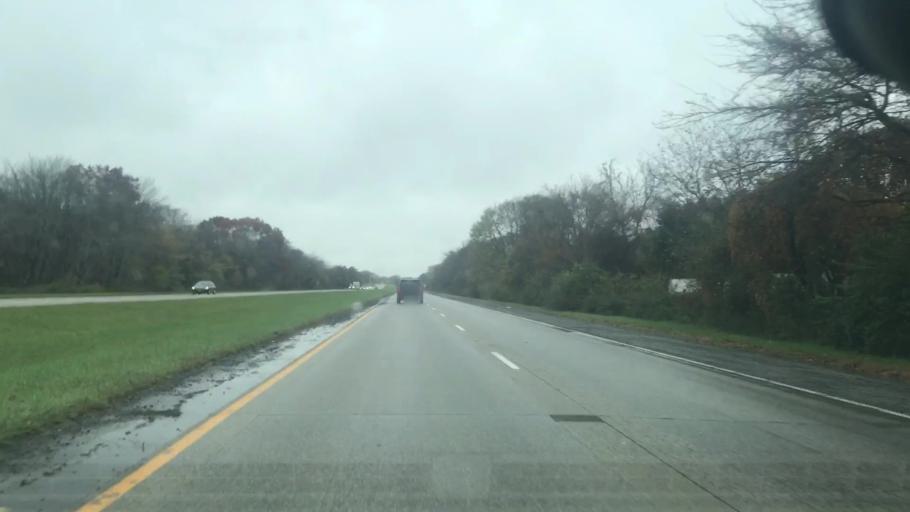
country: US
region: New York
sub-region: Suffolk County
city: West Islip
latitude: 40.7099
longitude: -73.3137
